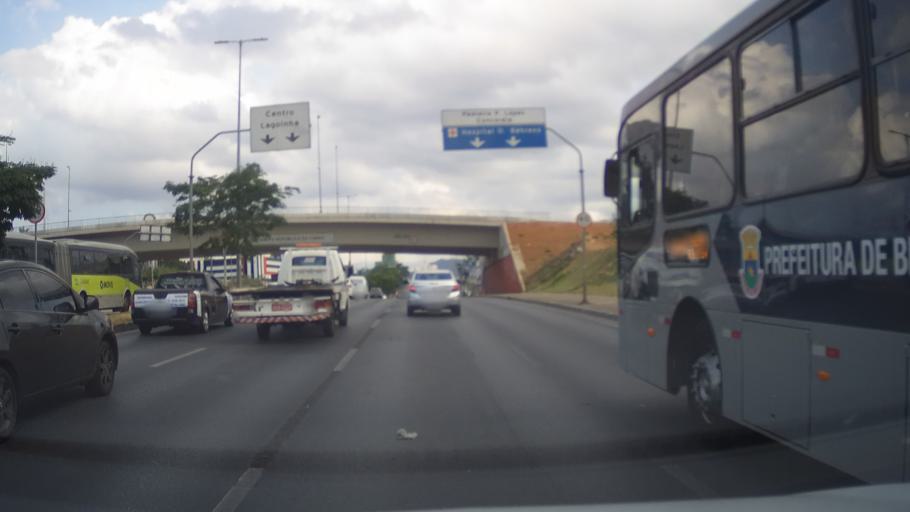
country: BR
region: Minas Gerais
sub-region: Belo Horizonte
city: Belo Horizonte
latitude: -19.8990
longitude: -43.9473
